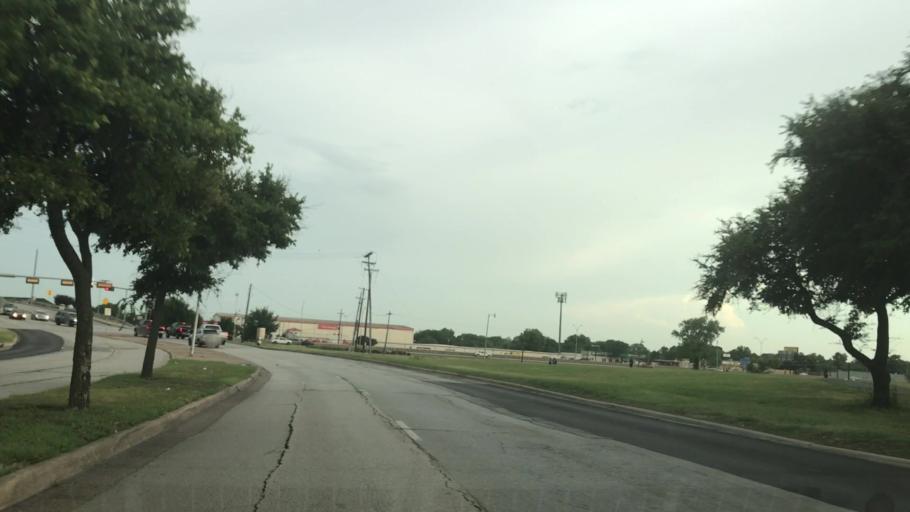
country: US
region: Texas
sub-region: Dallas County
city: Mesquite
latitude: 32.8118
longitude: -96.6567
